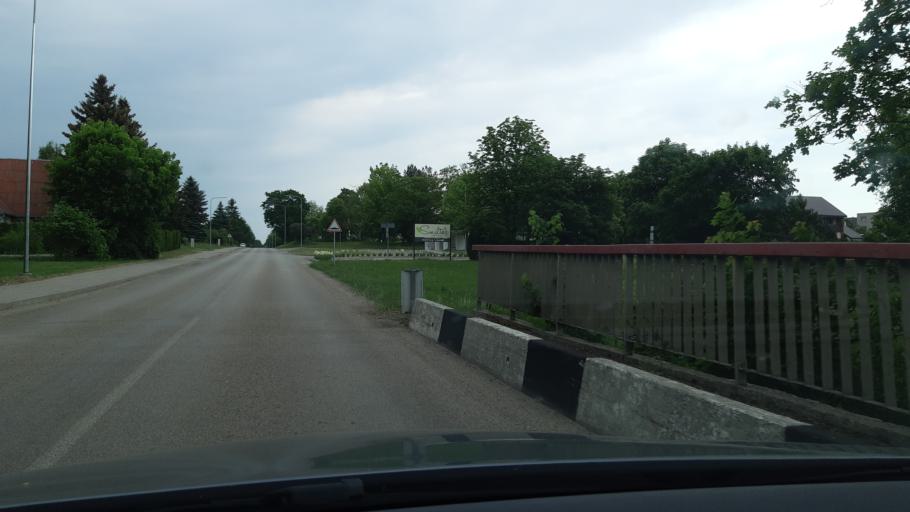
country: LT
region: Kauno apskritis
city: Kedainiai
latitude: 55.1928
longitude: 23.9008
